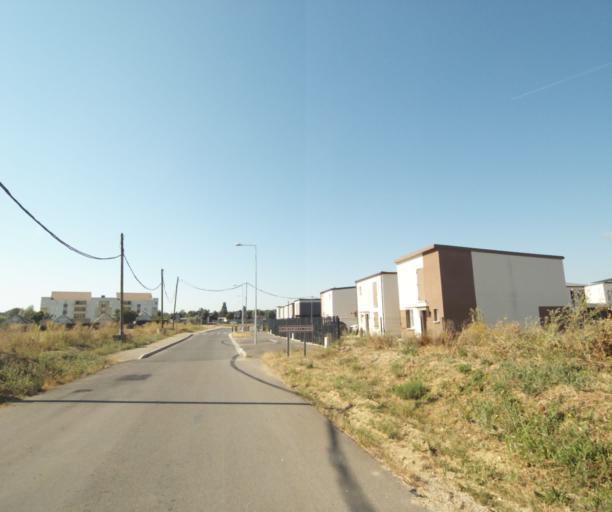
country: FR
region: Ile-de-France
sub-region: Departement de Seine-et-Marne
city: Moissy-Cramayel
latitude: 48.6343
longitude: 2.5866
